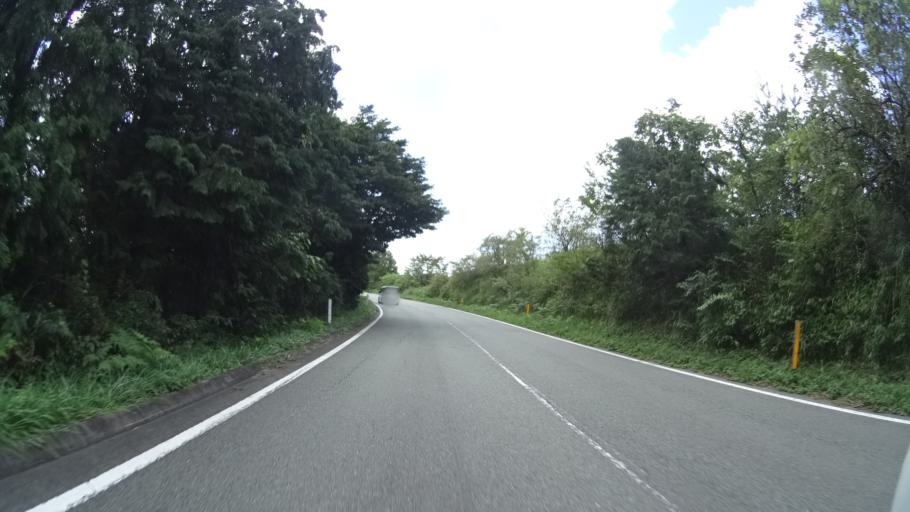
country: JP
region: Kumamoto
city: Aso
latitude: 33.0523
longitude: 131.1711
